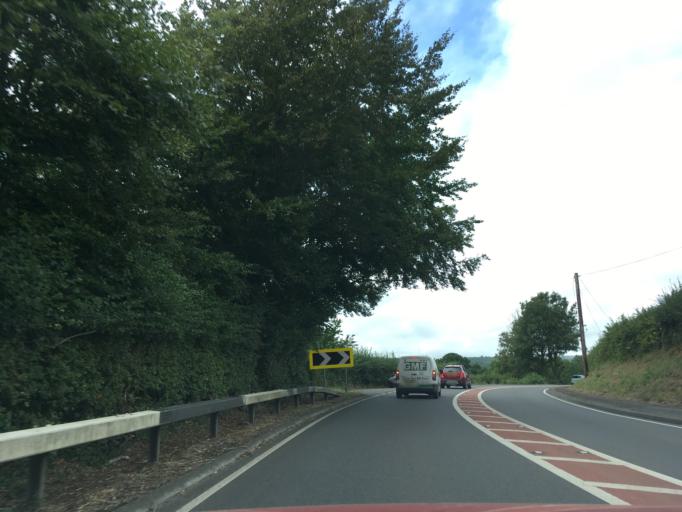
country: GB
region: Wales
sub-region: Carmarthenshire
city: Llanddarog
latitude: 51.8698
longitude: -4.1304
